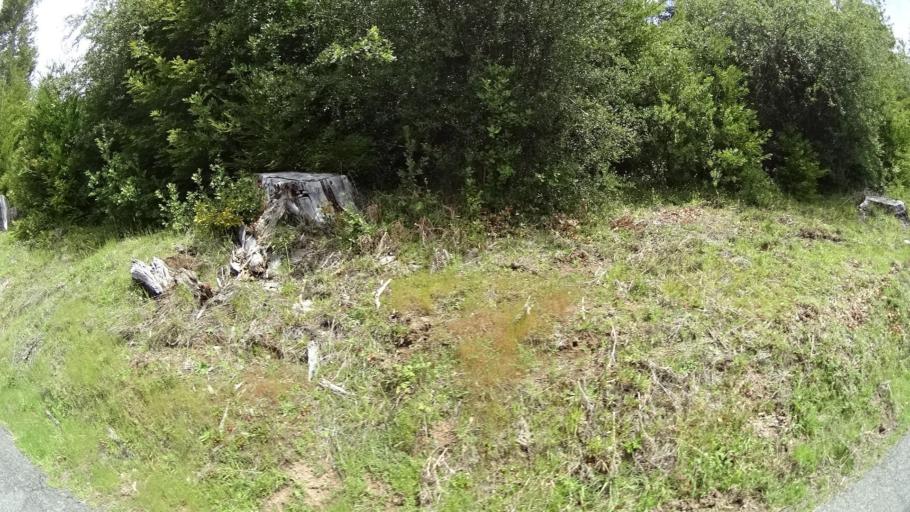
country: US
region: California
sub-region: Humboldt County
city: Blue Lake
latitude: 40.7866
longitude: -123.9657
